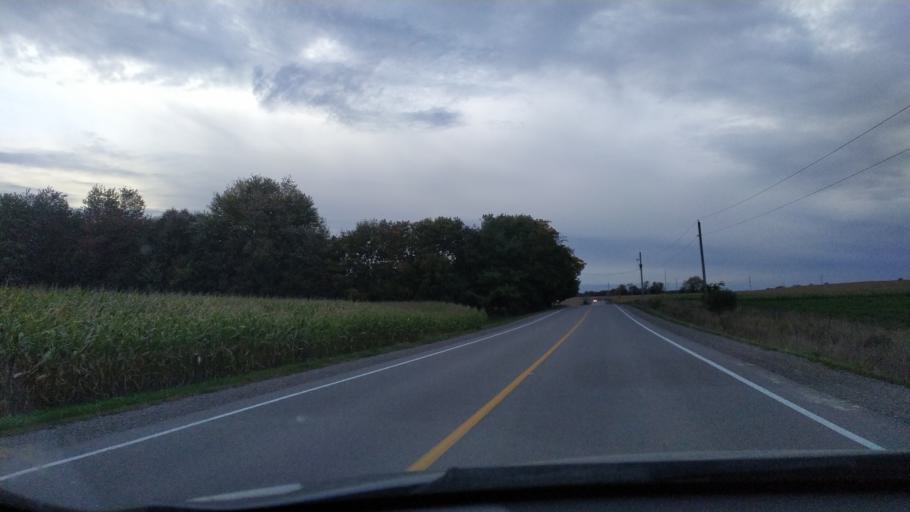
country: CA
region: Ontario
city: Waterloo
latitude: 43.4996
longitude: -80.6163
